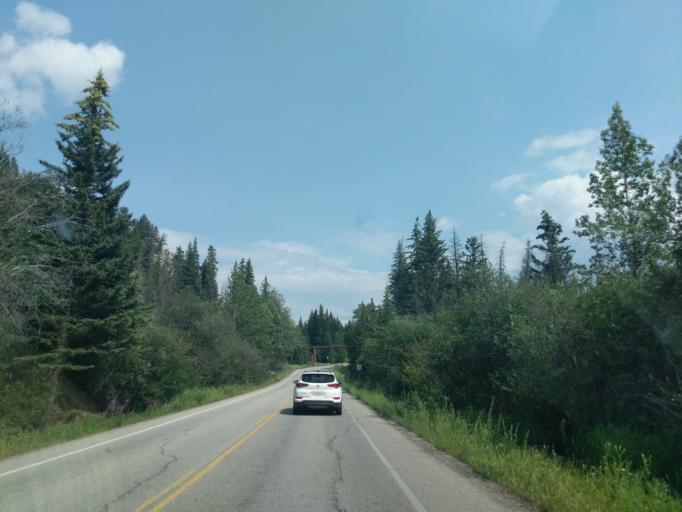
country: CA
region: Alberta
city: Banff
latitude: 51.1713
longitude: -115.6638
